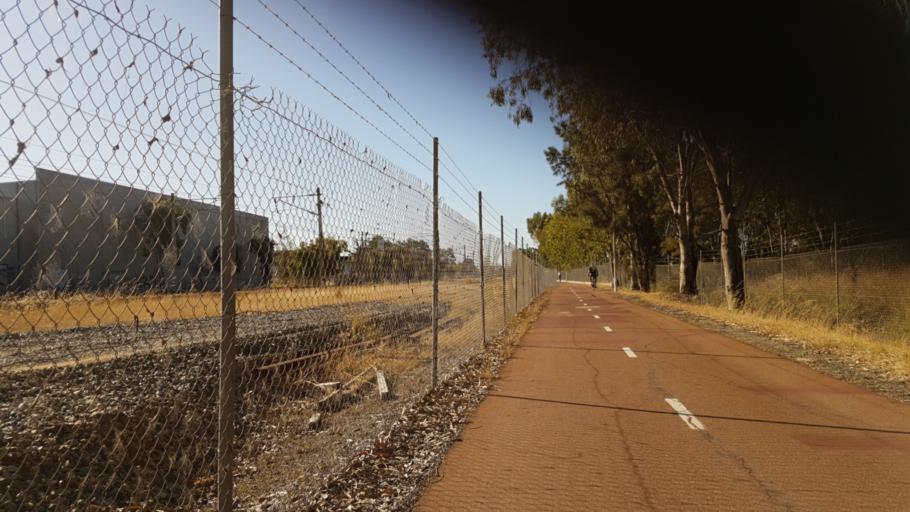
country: AU
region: Western Australia
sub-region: Gosnells
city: Kenwick
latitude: -32.0379
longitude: 115.9717
